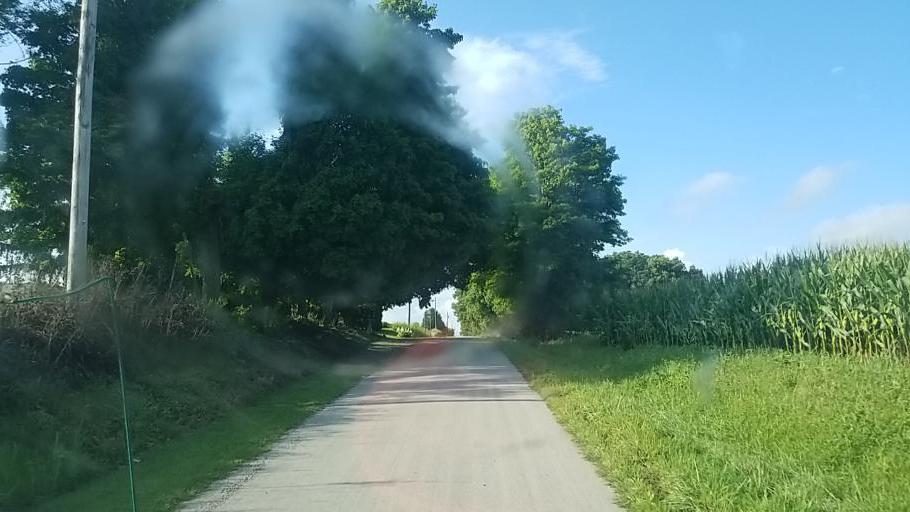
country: US
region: Ohio
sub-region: Wyandot County
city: Upper Sandusky
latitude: 40.8210
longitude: -83.1601
